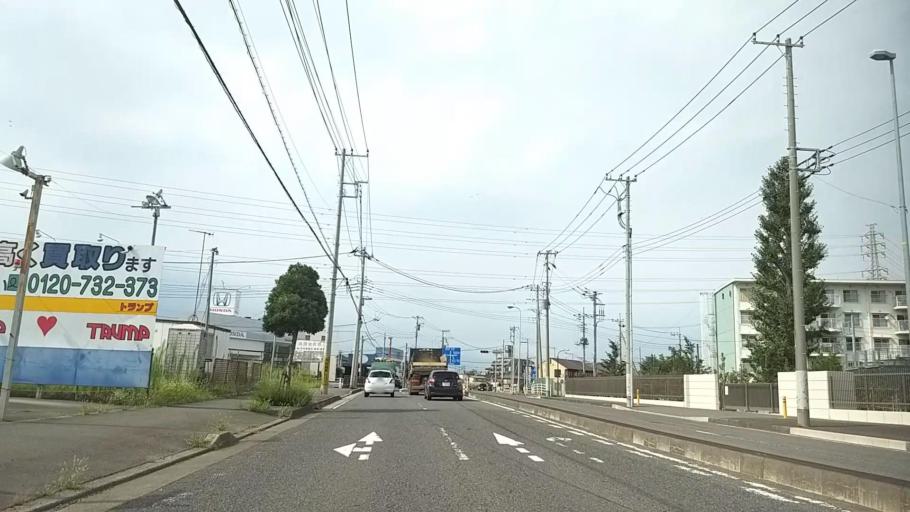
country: JP
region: Kanagawa
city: Atsugi
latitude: 35.4332
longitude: 139.3832
